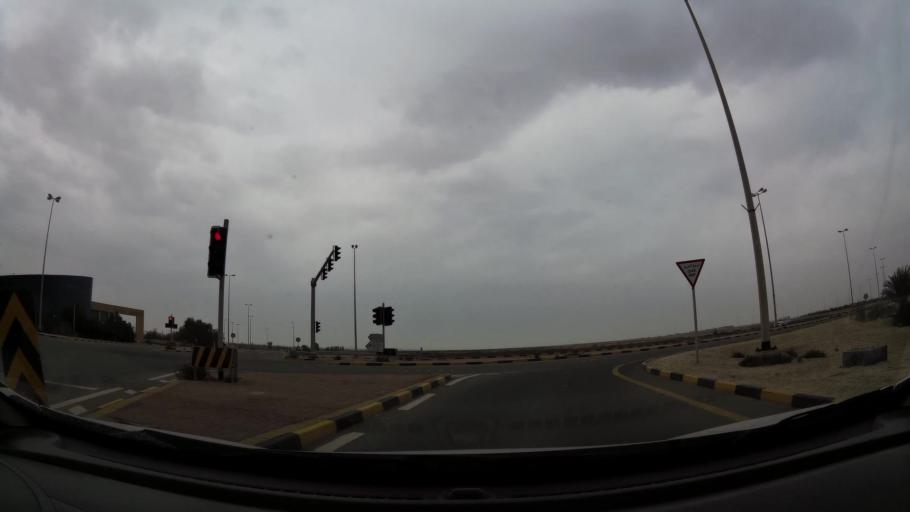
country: BH
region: Central Governorate
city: Dar Kulayb
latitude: 26.0165
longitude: 50.4862
